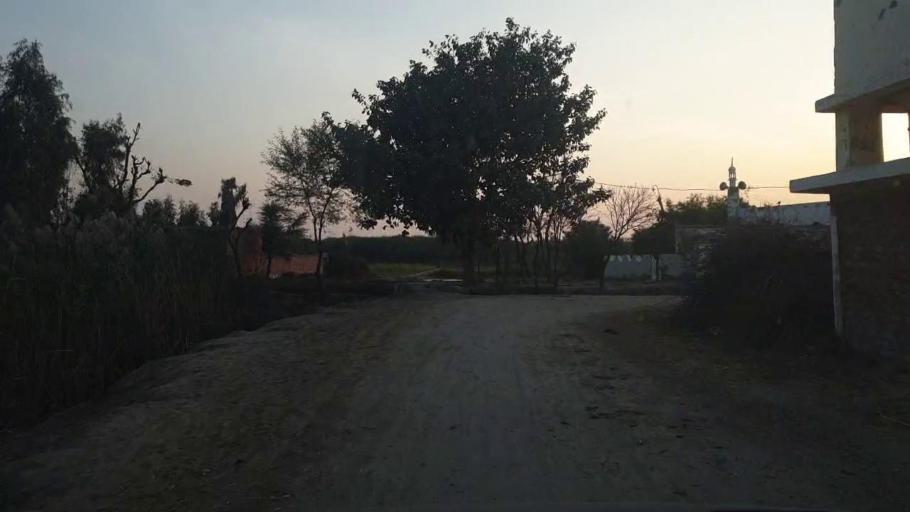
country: PK
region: Sindh
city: Bhit Shah
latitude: 25.8682
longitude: 68.5355
